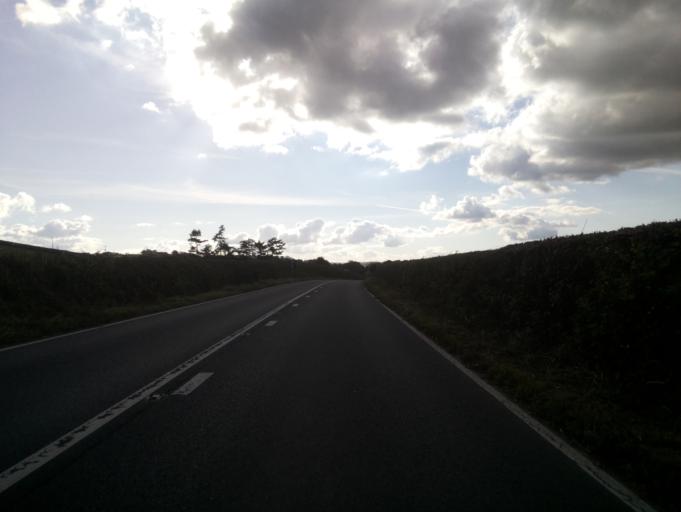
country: GB
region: Wales
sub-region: Sir Powys
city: Hay
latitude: 52.0623
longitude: -3.1558
